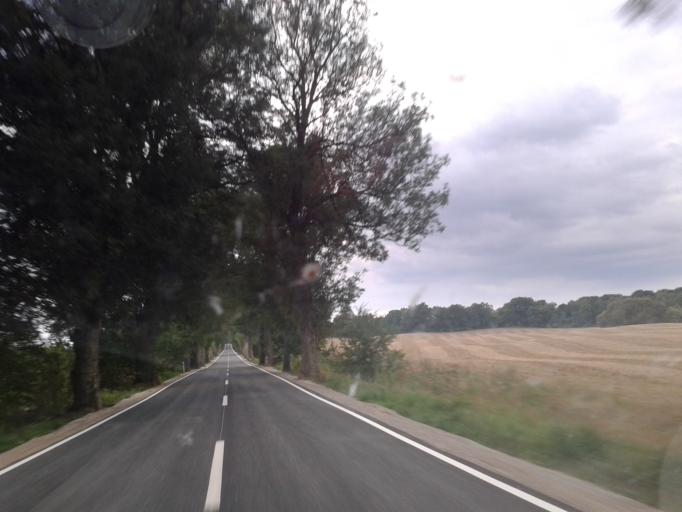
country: PL
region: West Pomeranian Voivodeship
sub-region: Powiat szczecinecki
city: Grzmiaca
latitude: 53.8603
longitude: 16.4764
